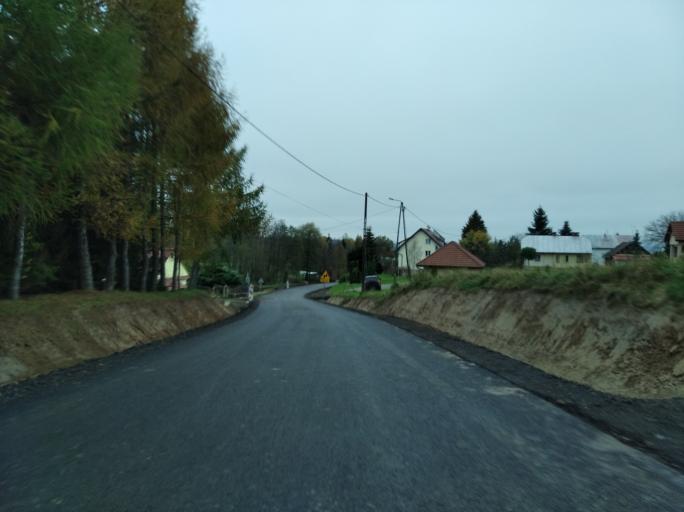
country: PL
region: Subcarpathian Voivodeship
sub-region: Powiat krosnienski
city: Odrzykon
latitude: 49.7360
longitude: 21.7724
